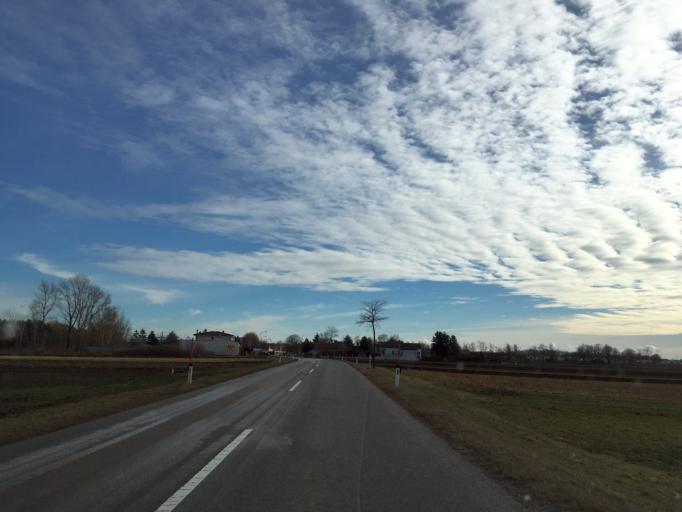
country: AT
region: Burgenland
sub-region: Politischer Bezirk Neusiedl am See
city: Pama
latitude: 48.0548
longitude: 17.0230
